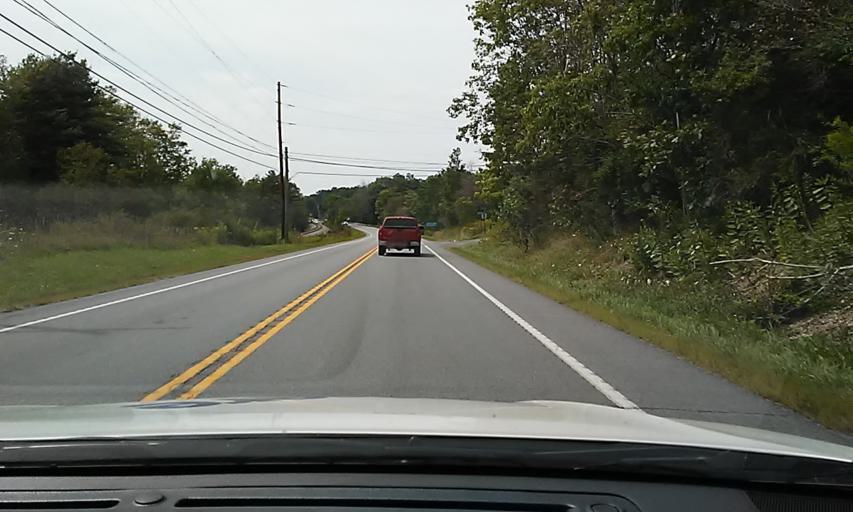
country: US
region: Pennsylvania
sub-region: Clearfield County
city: Treasure Lake
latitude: 41.1385
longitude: -78.6922
